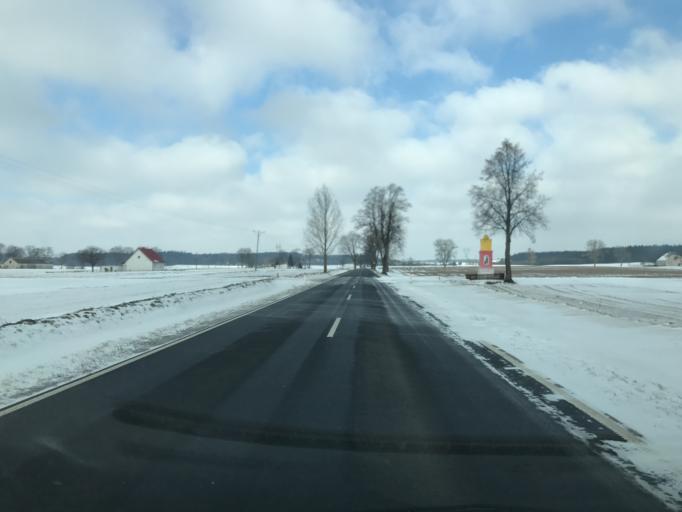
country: PL
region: Warmian-Masurian Voivodeship
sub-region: Powiat dzialdowski
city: Lidzbark
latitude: 53.3651
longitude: 19.8186
